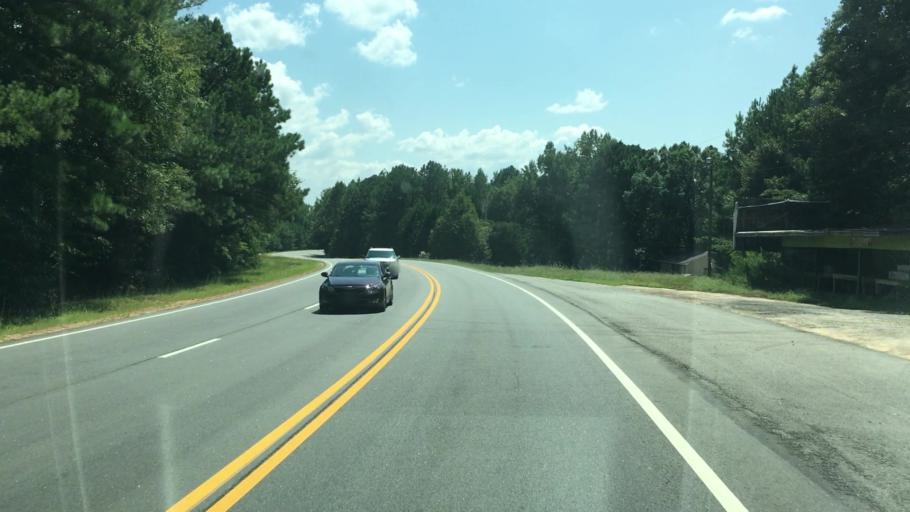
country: US
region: Georgia
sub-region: Morgan County
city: Madison
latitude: 33.7255
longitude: -83.4314
